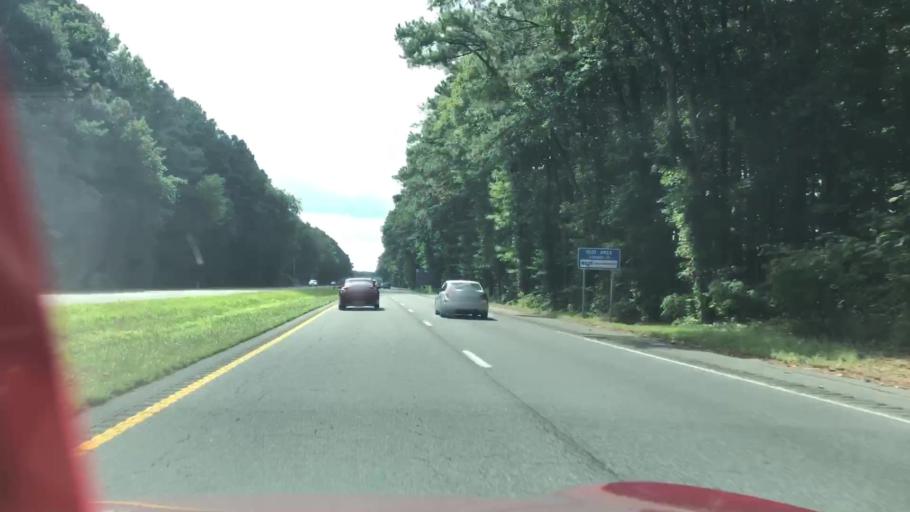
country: US
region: Virginia
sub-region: Accomack County
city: Wattsville
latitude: 37.9951
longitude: -75.5375
